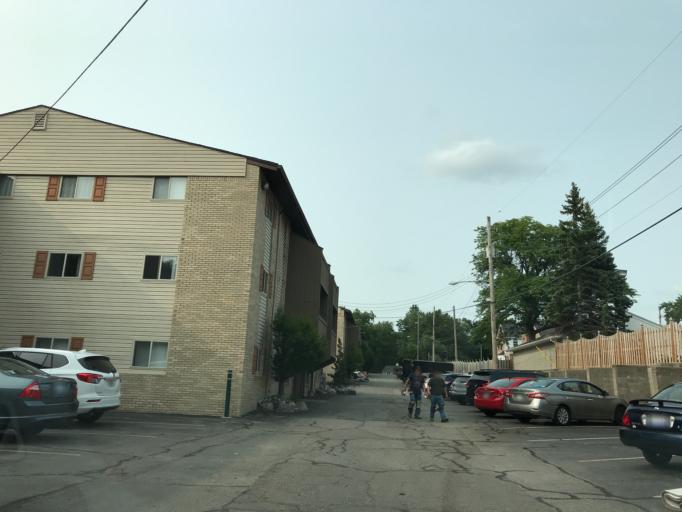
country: US
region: Michigan
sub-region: Ingham County
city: East Lansing
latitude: 42.7269
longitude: -84.4583
